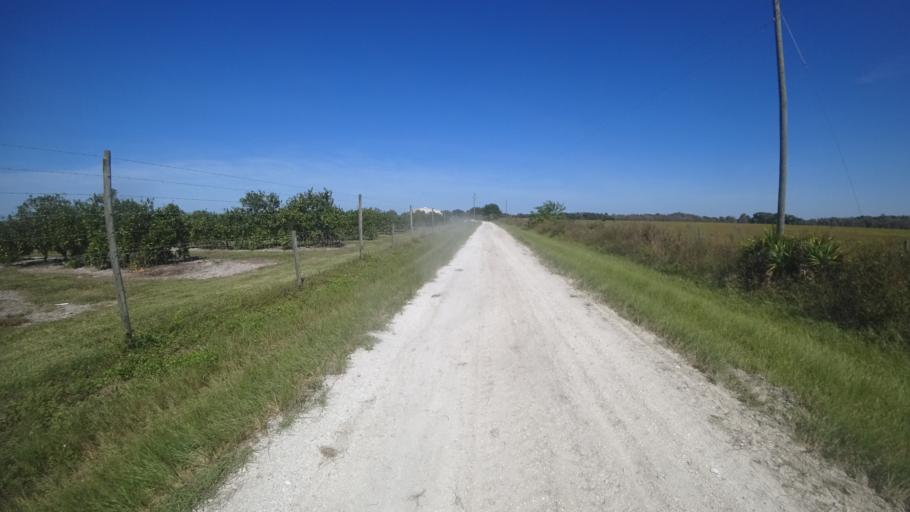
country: US
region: Florida
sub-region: Hardee County
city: Wauchula
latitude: 27.5325
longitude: -82.0876
